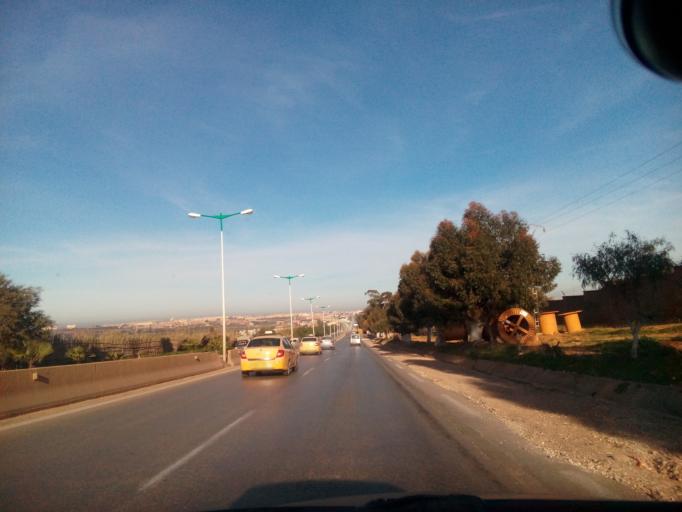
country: DZ
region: Mostaganem
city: Mostaganem
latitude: 35.8948
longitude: 0.1273
